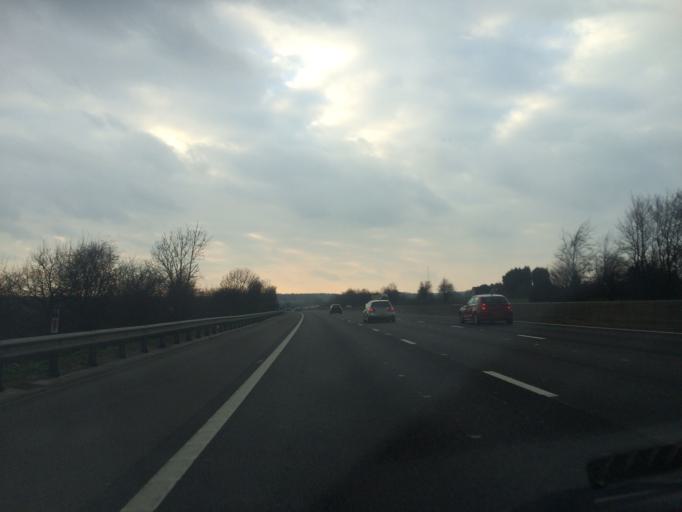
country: GB
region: England
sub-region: West Berkshire
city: Lambourn
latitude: 51.4699
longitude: -1.5214
